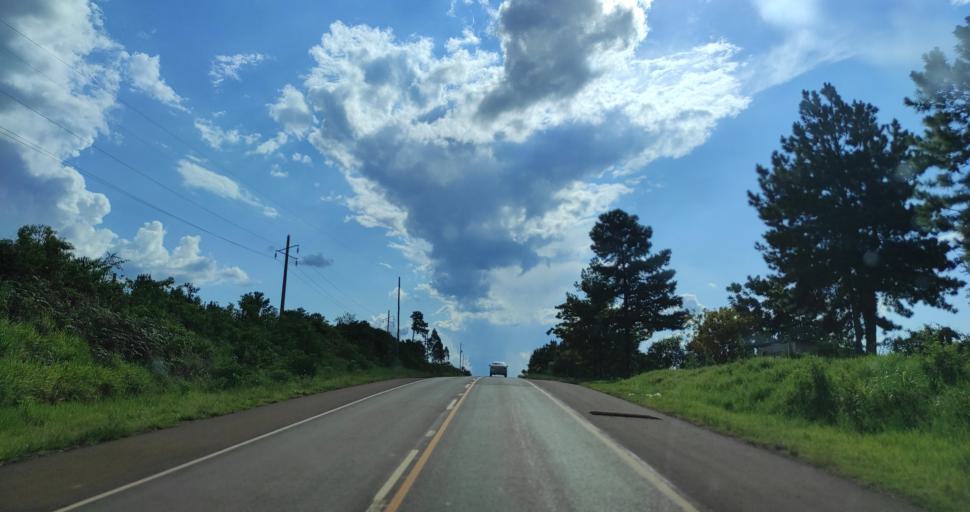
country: AR
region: Misiones
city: Bernardo de Irigoyen
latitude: -26.2945
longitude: -53.7777
